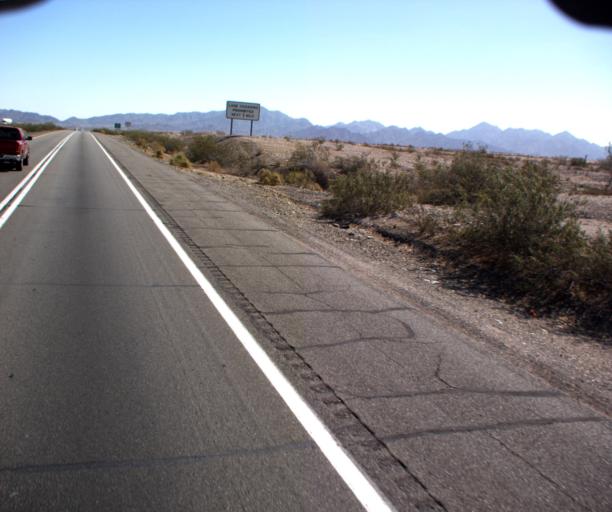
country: US
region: Arizona
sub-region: La Paz County
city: Ehrenberg
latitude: 33.6070
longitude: -114.4936
